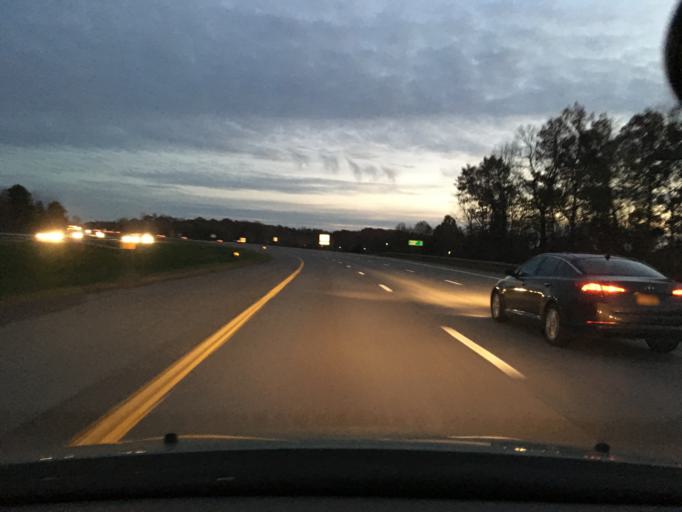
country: US
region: New York
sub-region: Monroe County
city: Fairport
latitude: 43.0414
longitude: -77.4625
